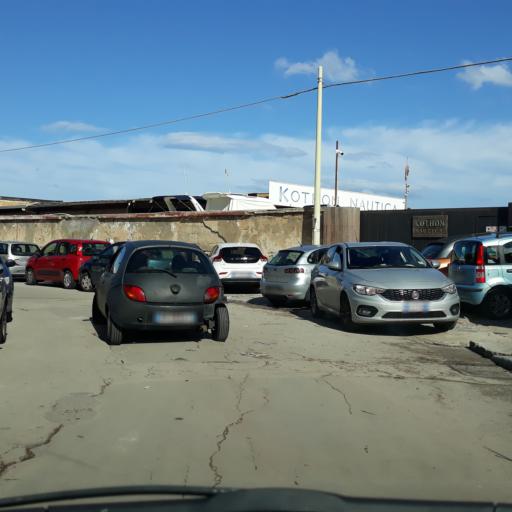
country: IT
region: Sicily
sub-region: Palermo
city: Palermo
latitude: 38.1595
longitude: 13.3717
